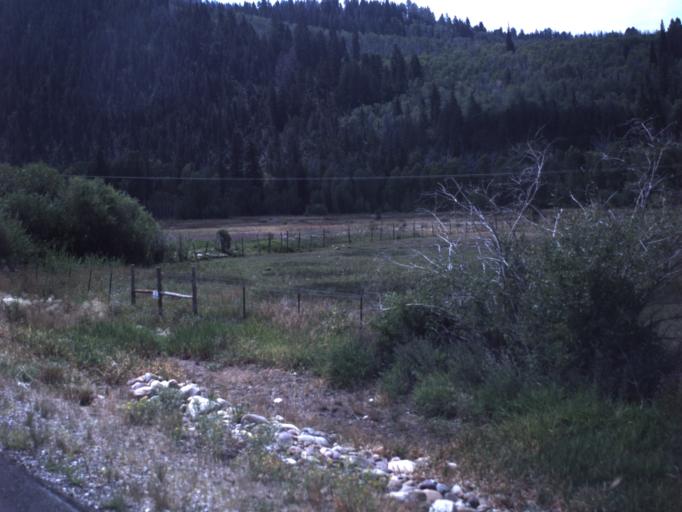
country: US
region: Utah
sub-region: Summit County
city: Francis
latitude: 40.5548
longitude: -111.1619
